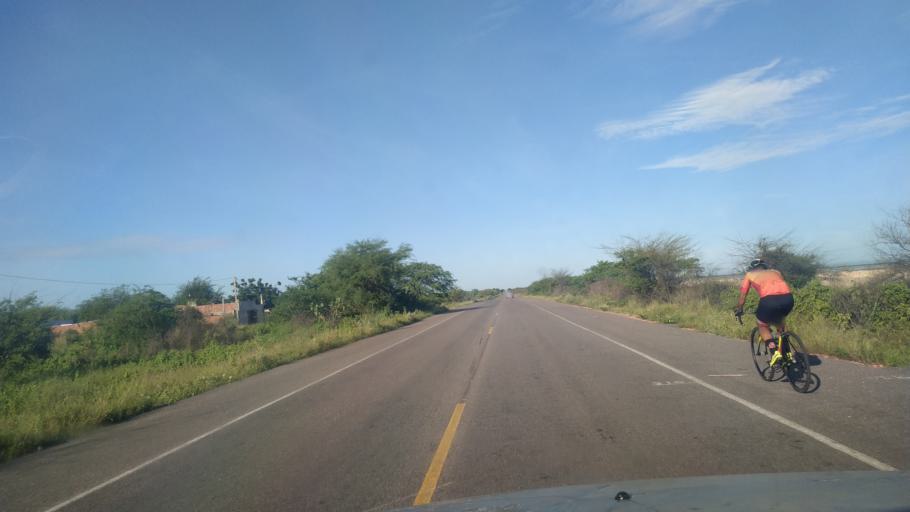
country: BR
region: Rio Grande do Norte
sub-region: Areia Branca
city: Areia Branca
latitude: -5.0457
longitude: -37.1430
